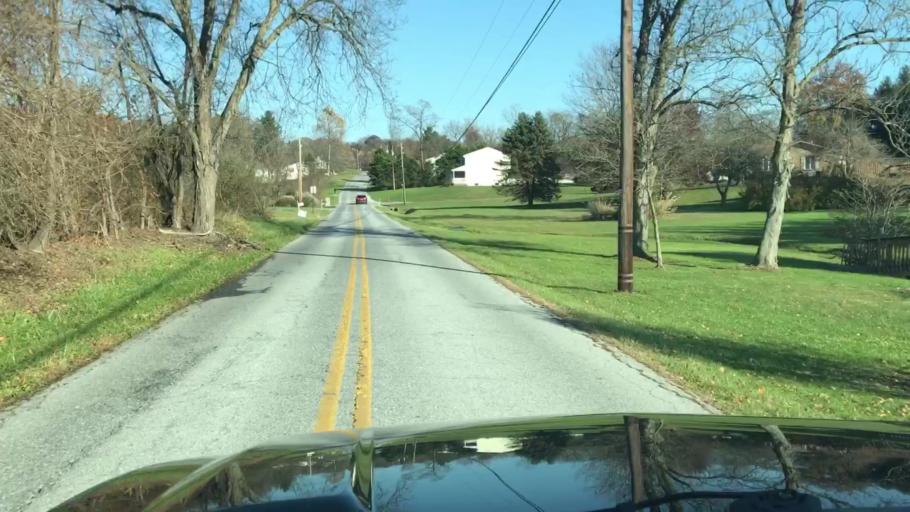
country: US
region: Pennsylvania
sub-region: Cumberland County
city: Lower Allen
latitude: 40.1582
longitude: -76.8807
